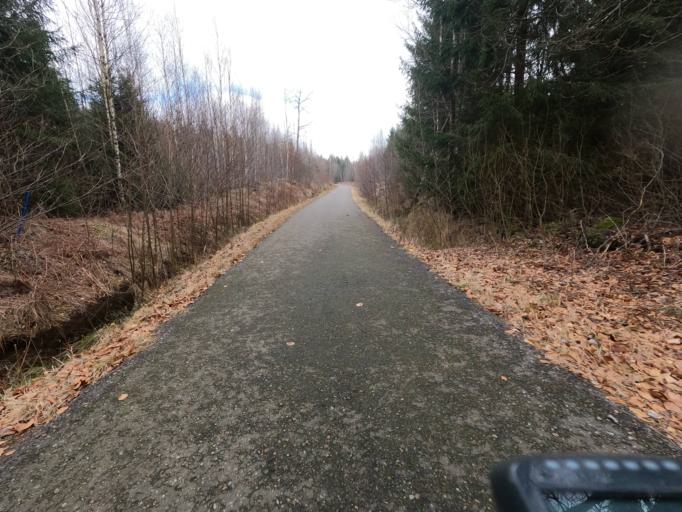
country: SE
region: Joenkoeping
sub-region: Varnamo Kommun
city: Rydaholm
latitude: 56.8382
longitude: 14.2396
